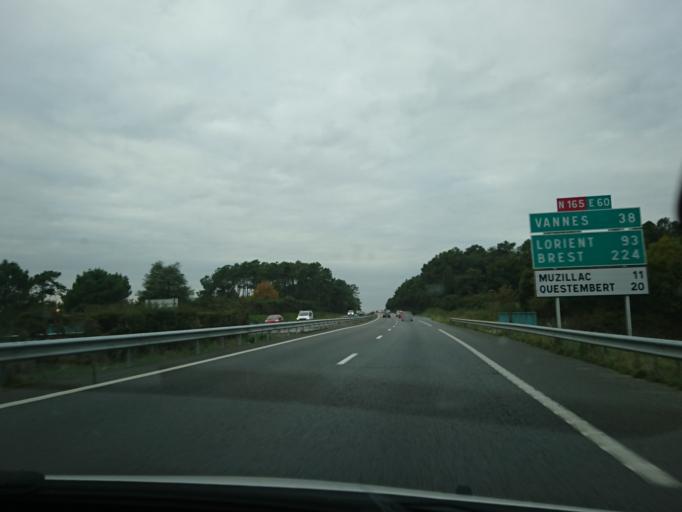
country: FR
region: Brittany
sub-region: Departement du Morbihan
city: Marzan
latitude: 47.5361
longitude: -2.3409
